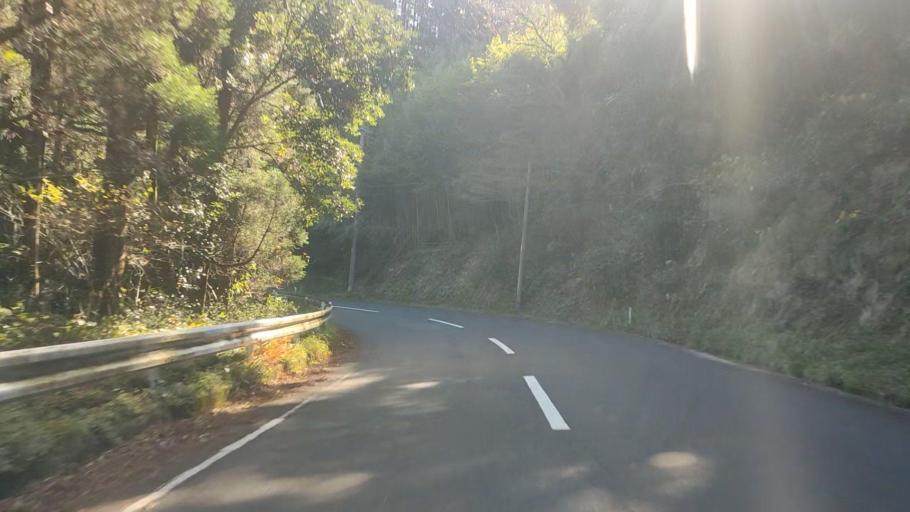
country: JP
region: Kagoshima
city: Kokubu-matsuki
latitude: 31.6676
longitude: 130.8268
